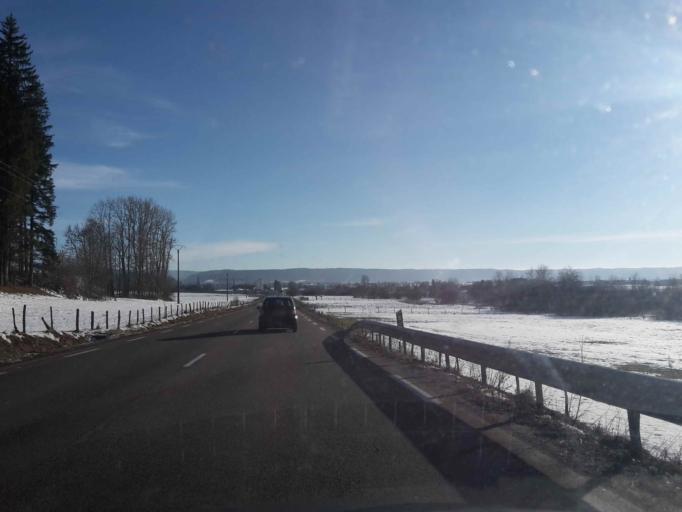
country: FR
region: Franche-Comte
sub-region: Departement du Doubs
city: Doubs
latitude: 46.9532
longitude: 6.3419
